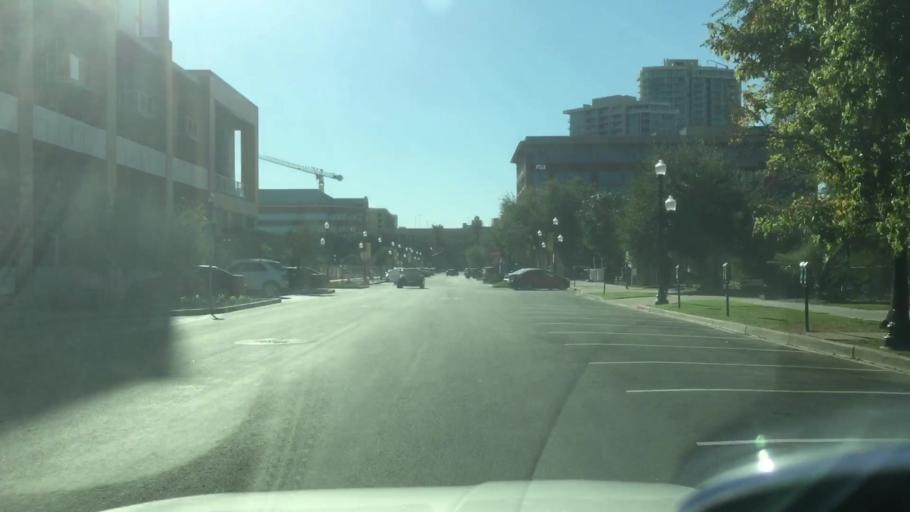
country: US
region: Arizona
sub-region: Maricopa County
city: Tempe Junction
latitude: 33.4232
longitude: -111.9373
